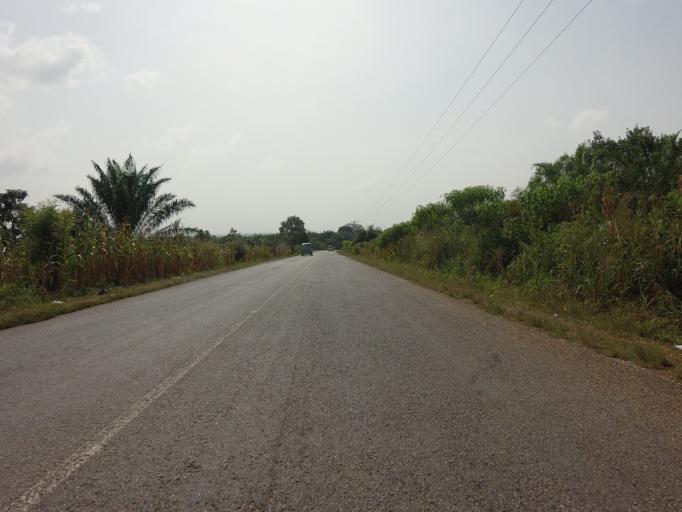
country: GH
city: Akropong
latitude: 6.2714
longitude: 0.1355
